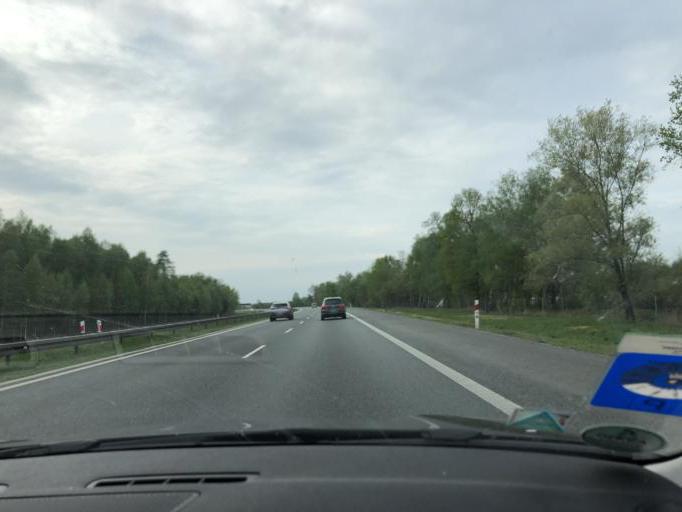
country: PL
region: Opole Voivodeship
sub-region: Powiat brzeski
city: Lewin Brzeski
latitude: 50.7017
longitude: 17.6181
